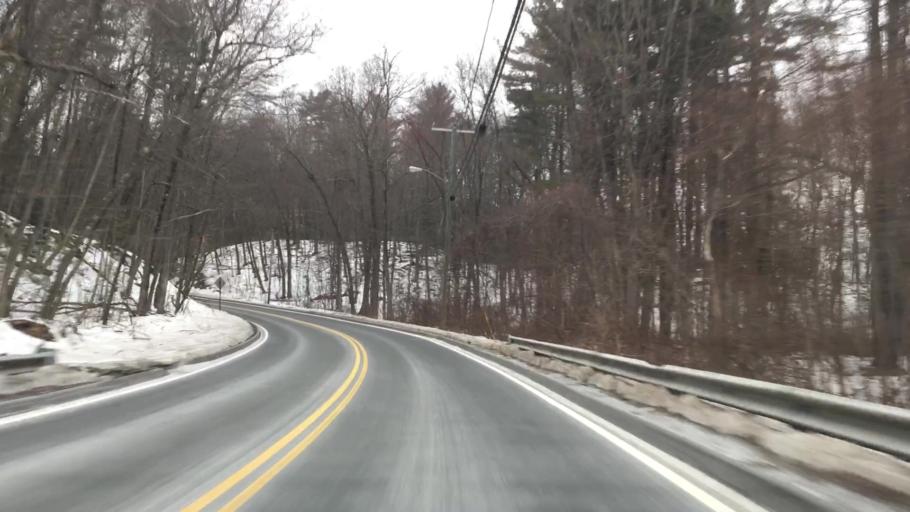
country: US
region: Massachusetts
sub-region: Hampden County
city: West Springfield
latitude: 42.0975
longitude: -72.6829
